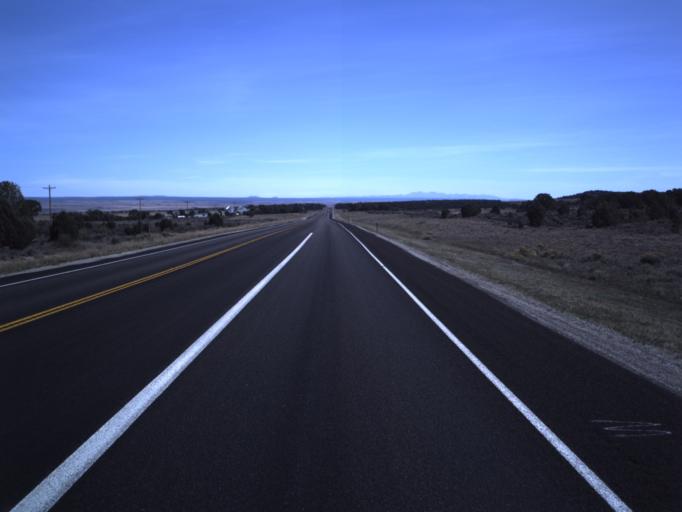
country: US
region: Colorado
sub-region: Dolores County
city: Dove Creek
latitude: 37.8377
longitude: -109.1161
